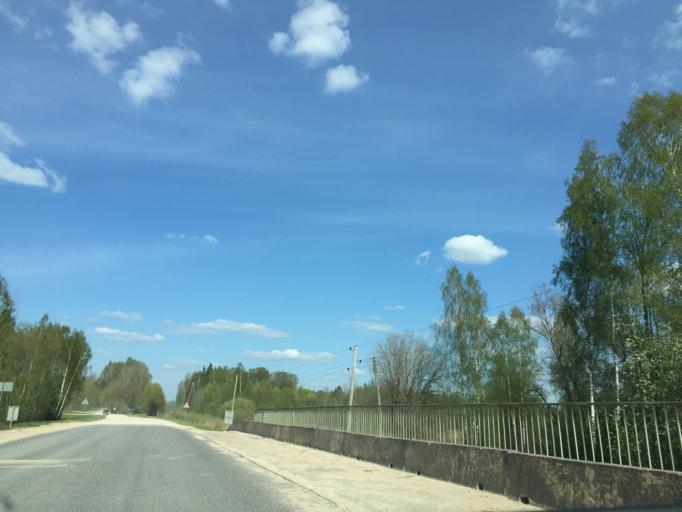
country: LV
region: Vecumnieki
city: Vecumnieki
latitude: 56.5067
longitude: 24.3981
